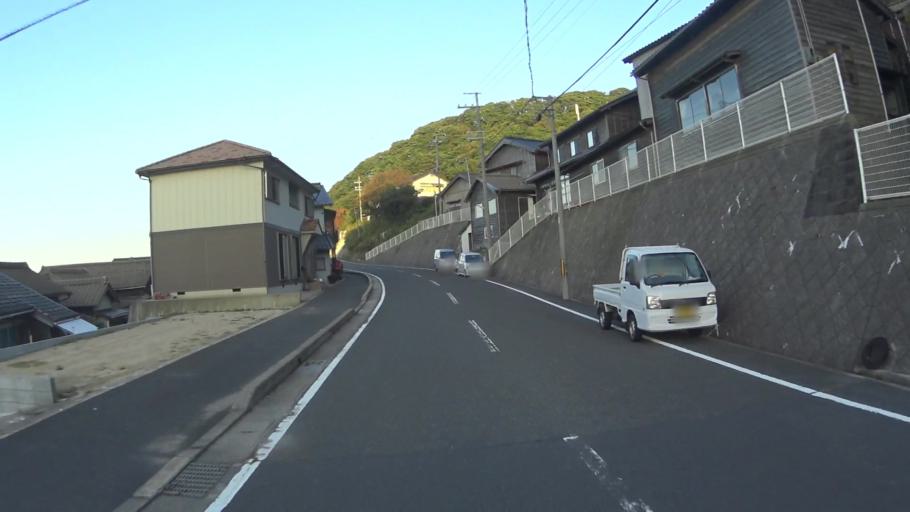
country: JP
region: Hyogo
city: Toyooka
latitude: 35.6894
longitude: 134.9945
